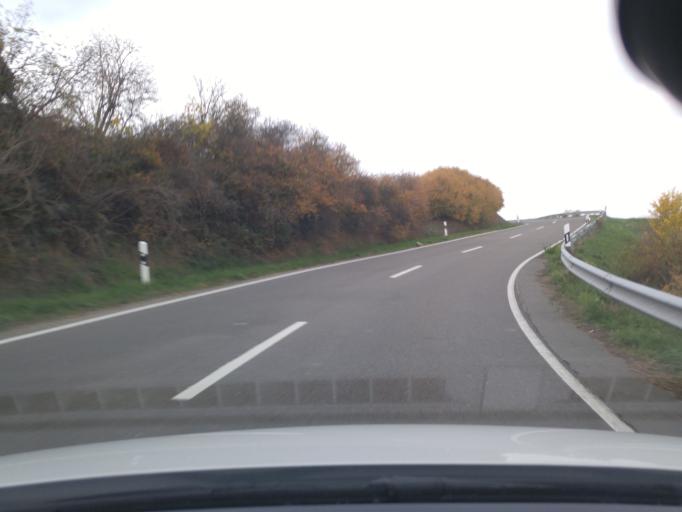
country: DE
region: Rheinland-Pfalz
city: Frankweiler
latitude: 49.2231
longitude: 8.0466
